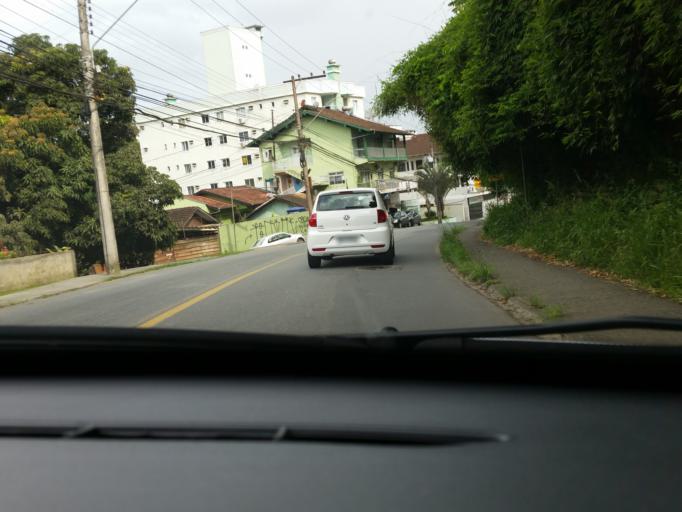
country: BR
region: Santa Catarina
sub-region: Blumenau
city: Blumenau
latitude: -26.9100
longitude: -49.1060
